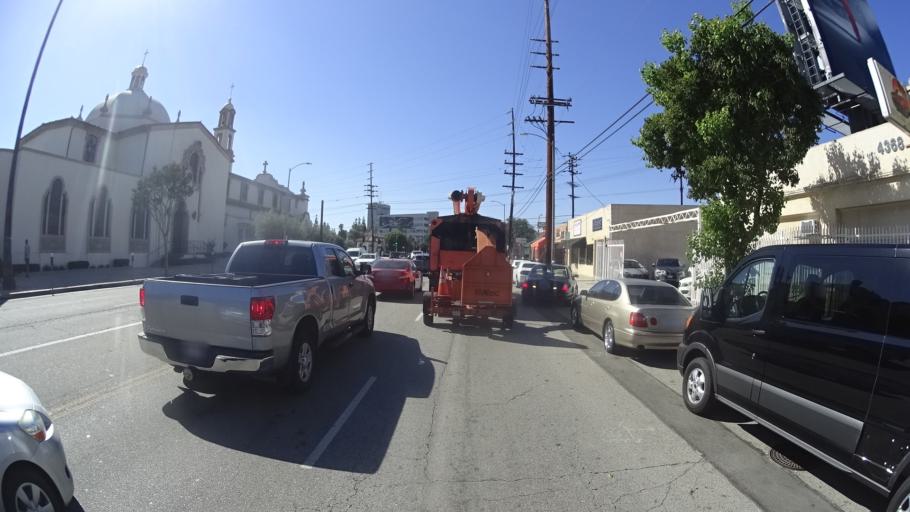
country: US
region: California
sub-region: Los Angeles County
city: Universal City
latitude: 34.1498
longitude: -118.3654
